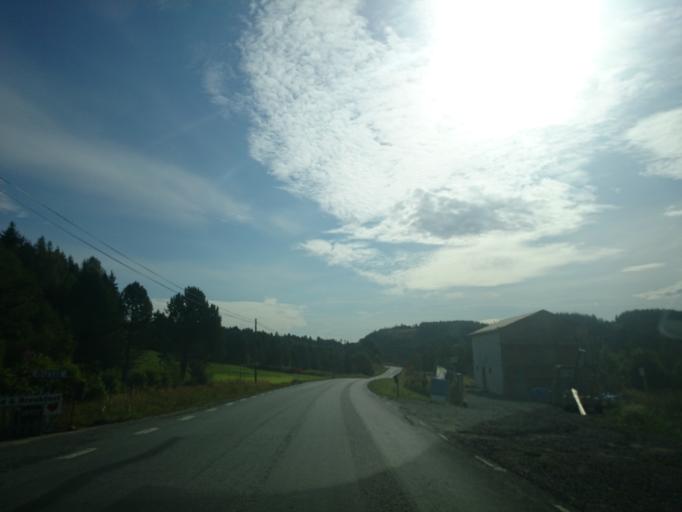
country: SE
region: Vaesternorrland
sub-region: Kramfors Kommun
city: Nordingra
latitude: 62.9227
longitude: 18.1898
